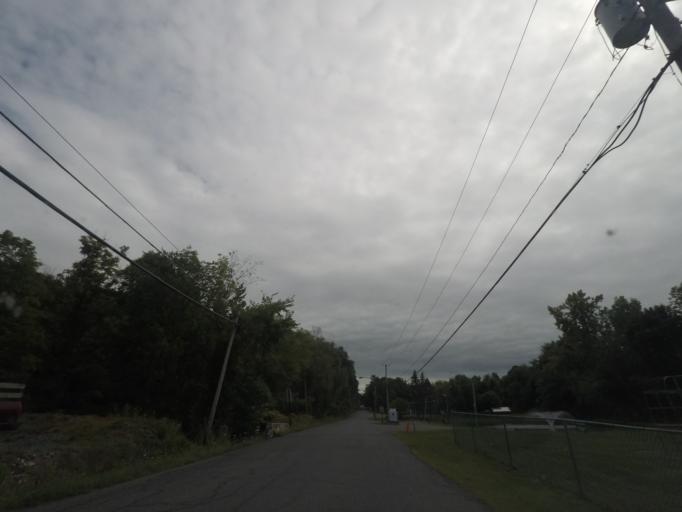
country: US
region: New York
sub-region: Rensselaer County
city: Nassau
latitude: 42.5133
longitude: -73.6093
